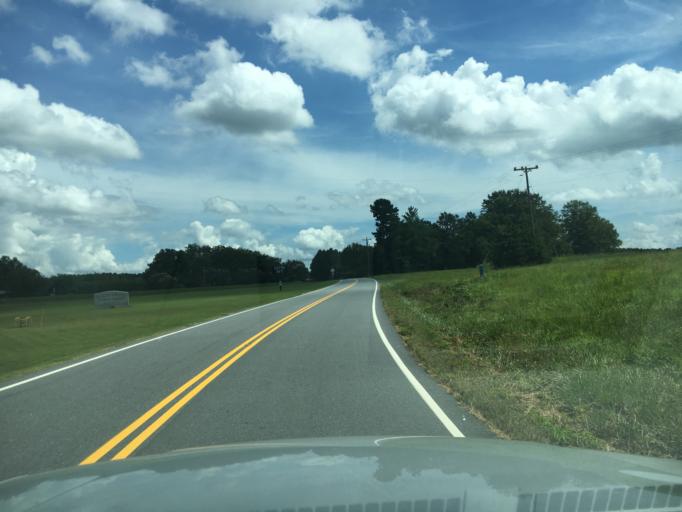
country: US
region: South Carolina
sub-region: Anderson County
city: Belton
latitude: 34.5365
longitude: -82.4374
